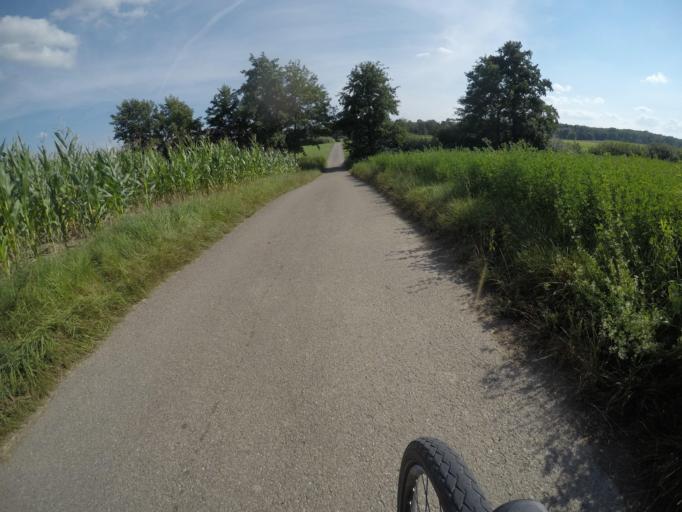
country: DE
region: Baden-Wuerttemberg
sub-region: Karlsruhe Region
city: Olbronn-Durrn
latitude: 48.9653
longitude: 8.7525
